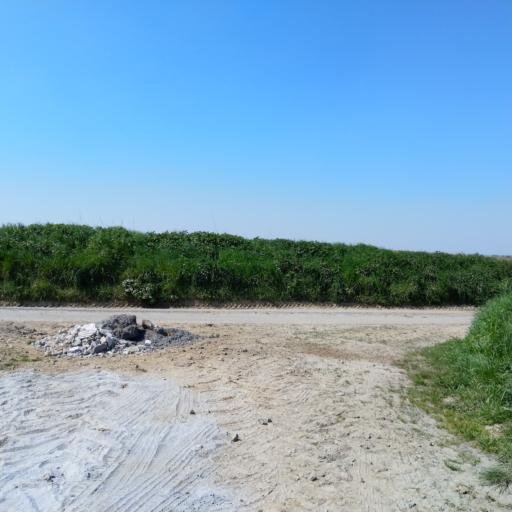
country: BE
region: Wallonia
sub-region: Province du Hainaut
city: Lens
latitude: 50.5633
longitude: 3.8837
